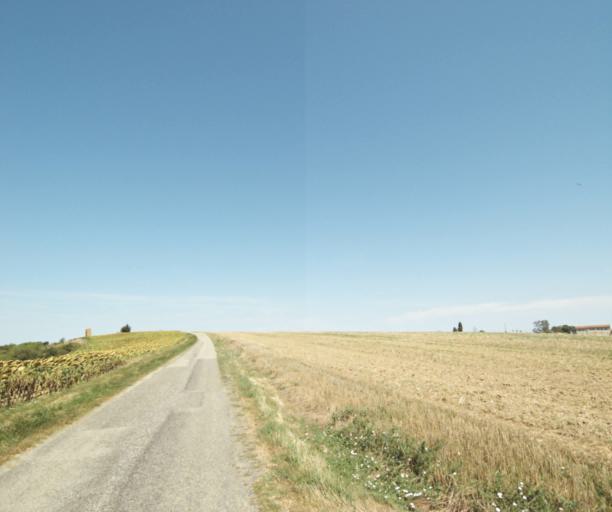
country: FR
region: Midi-Pyrenees
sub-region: Departement de l'Ariege
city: Lezat-sur-Leze
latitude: 43.2674
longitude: 1.3782
